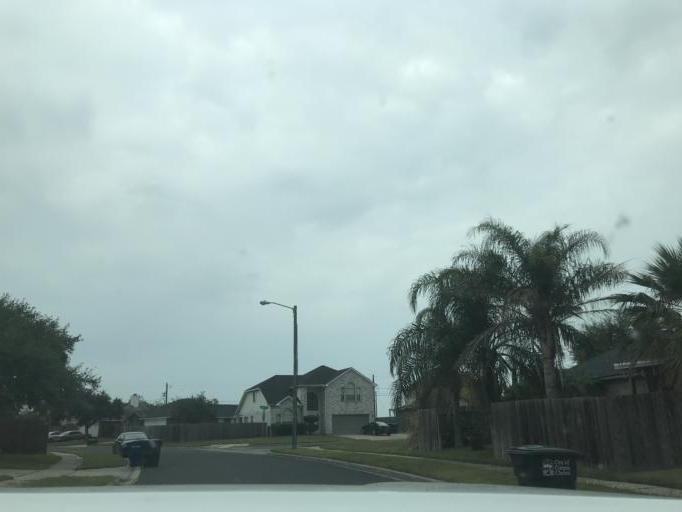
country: US
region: Texas
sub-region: Nueces County
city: Corpus Christi
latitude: 27.6684
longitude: -97.3434
